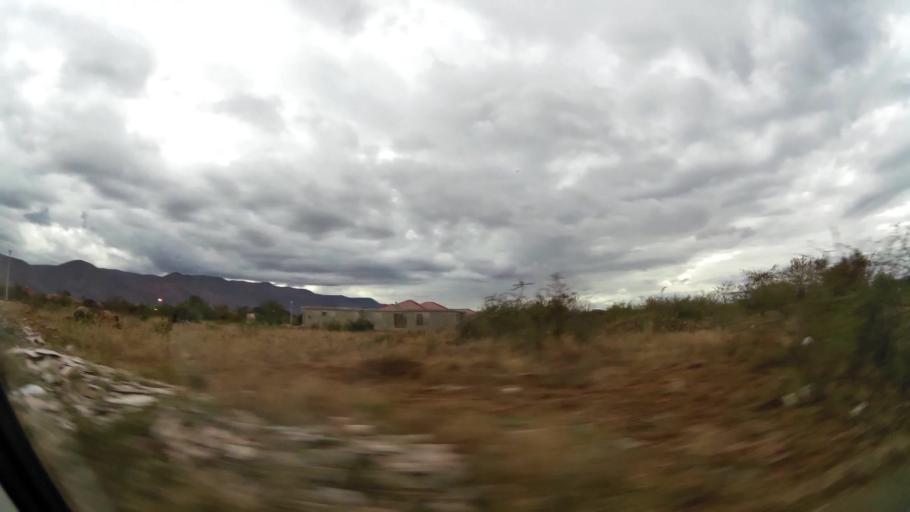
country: ZA
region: Limpopo
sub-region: Waterberg District Municipality
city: Mokopane
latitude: -24.1973
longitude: 28.9985
